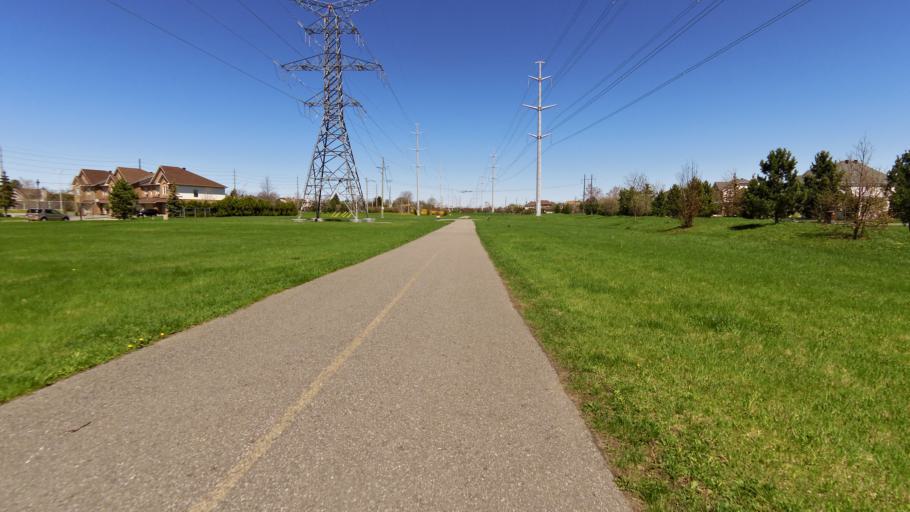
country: CA
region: Ontario
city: Clarence-Rockland
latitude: 45.4622
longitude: -75.4790
